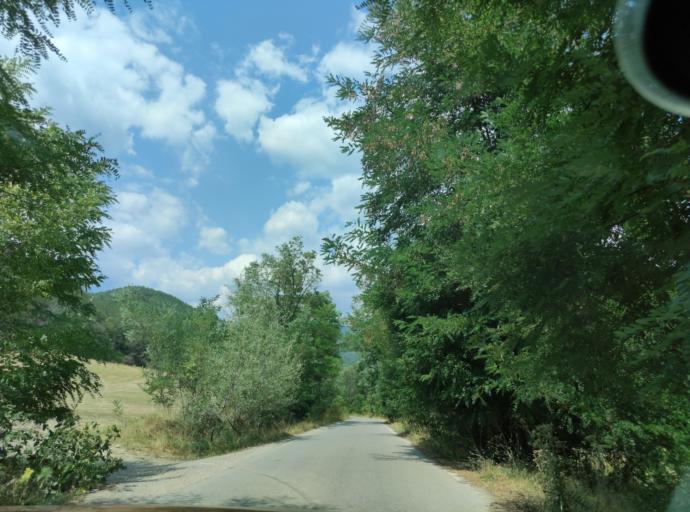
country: BG
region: Blagoevgrad
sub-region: Obshtina Belitsa
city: Belitsa
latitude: 41.9888
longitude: 23.5527
